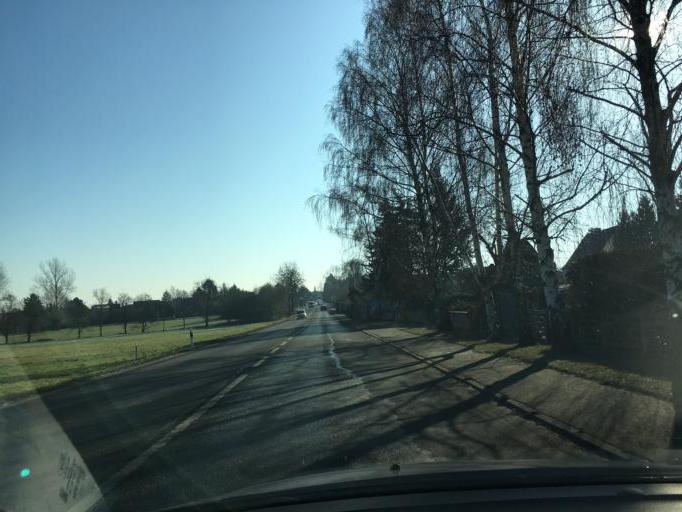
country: DE
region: Saxony
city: Grossposna
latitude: 51.2648
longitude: 12.4998
